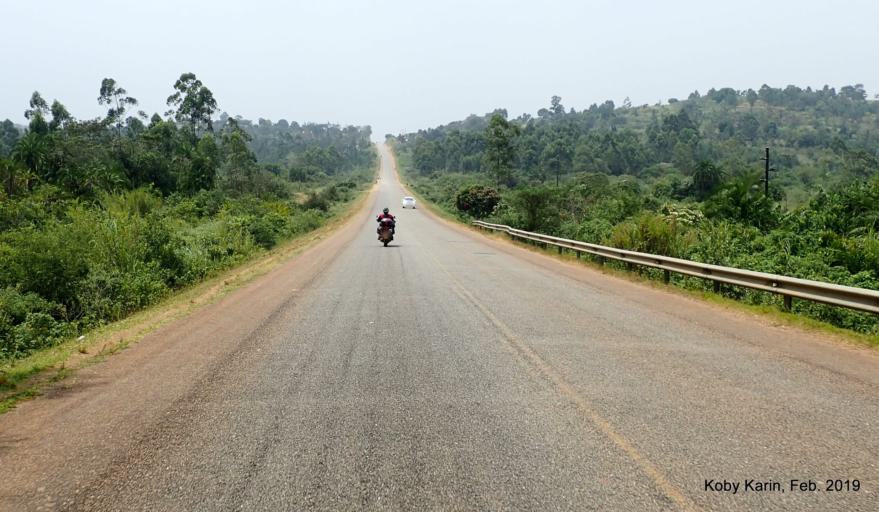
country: UG
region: Western Region
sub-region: Kyegegwa District
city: Kyegegwa
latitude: 0.5137
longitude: 30.9752
